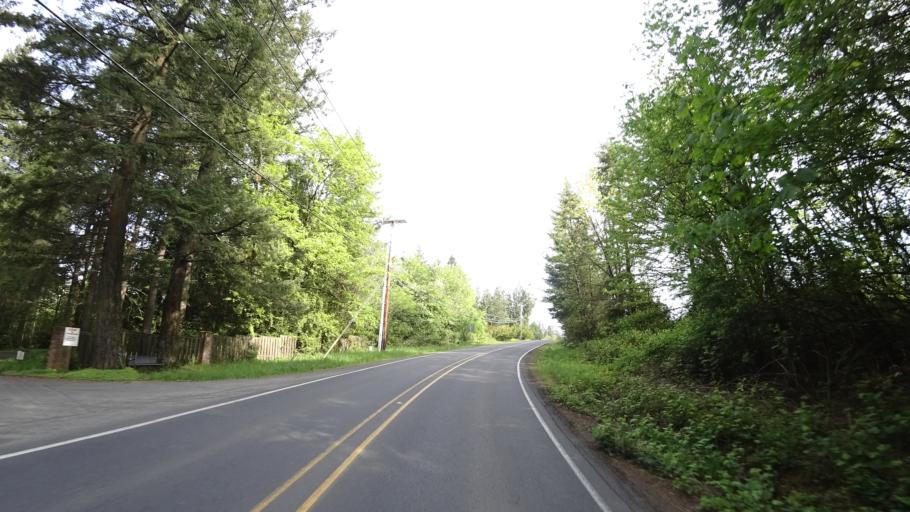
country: US
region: Oregon
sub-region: Washington County
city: Aloha
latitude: 45.4401
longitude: -122.8566
